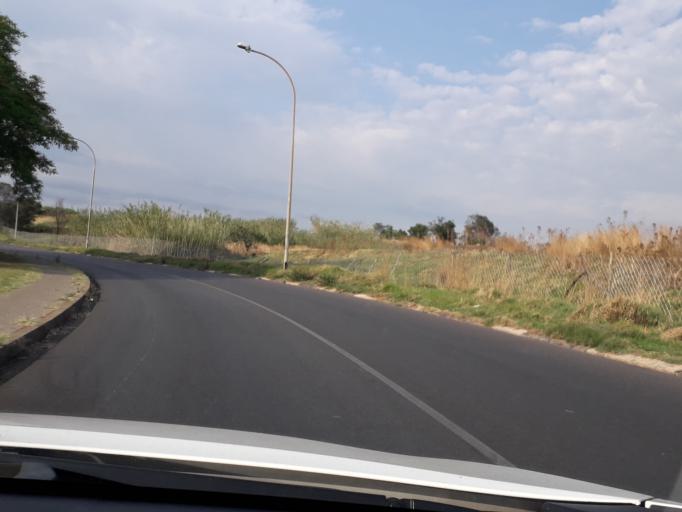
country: ZA
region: Gauteng
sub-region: City of Johannesburg Metropolitan Municipality
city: Johannesburg
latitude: -26.1673
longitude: 27.9756
